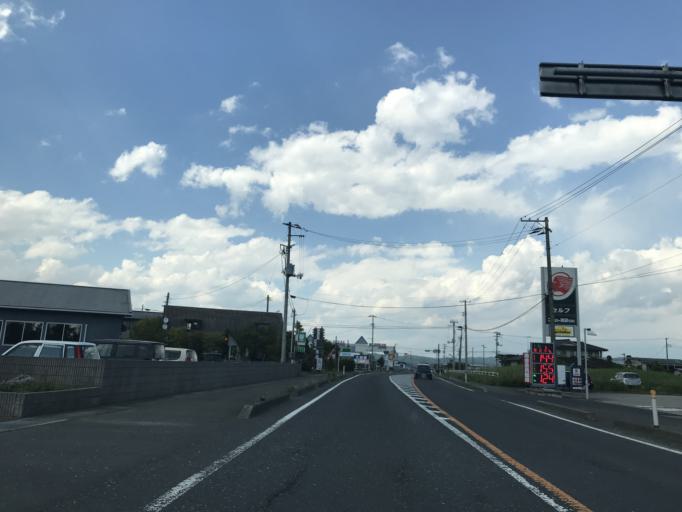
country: JP
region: Miyagi
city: Wakuya
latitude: 38.5071
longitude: 141.1207
